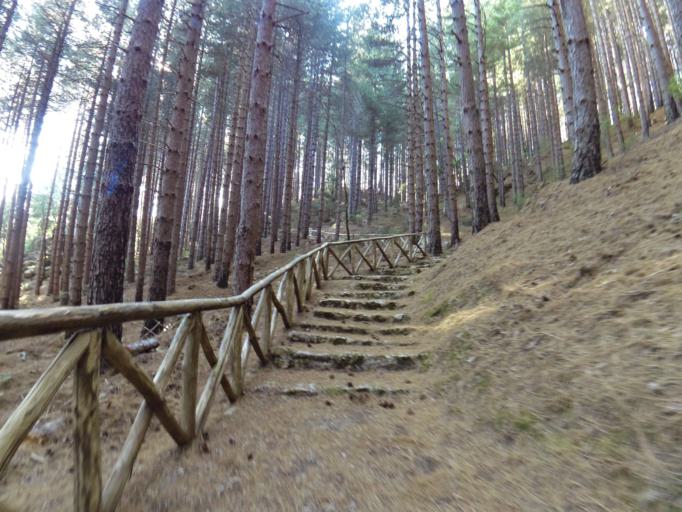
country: IT
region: Calabria
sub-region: Provincia di Vibo-Valentia
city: Nardodipace
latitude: 38.4622
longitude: 16.3490
